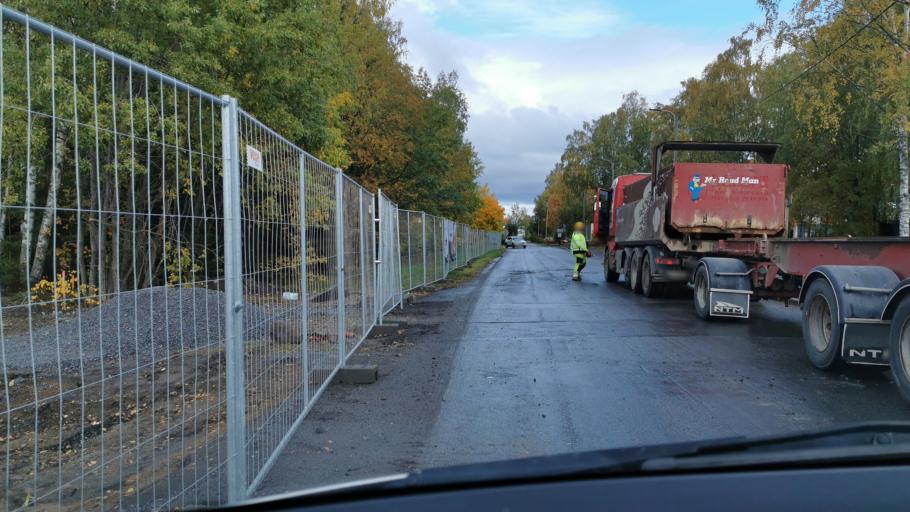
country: FI
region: Ostrobothnia
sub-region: Vaasa
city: Vaasa
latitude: 63.0915
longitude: 21.5636
